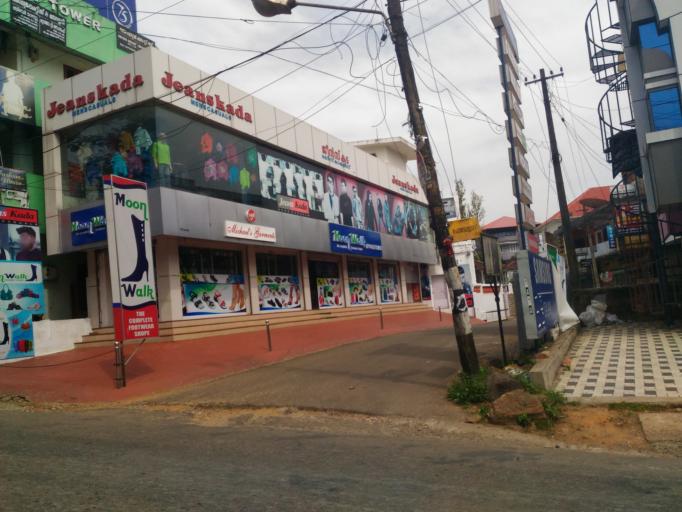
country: IN
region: Kerala
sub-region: Kottayam
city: Lalam
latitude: 9.7134
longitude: 76.6832
